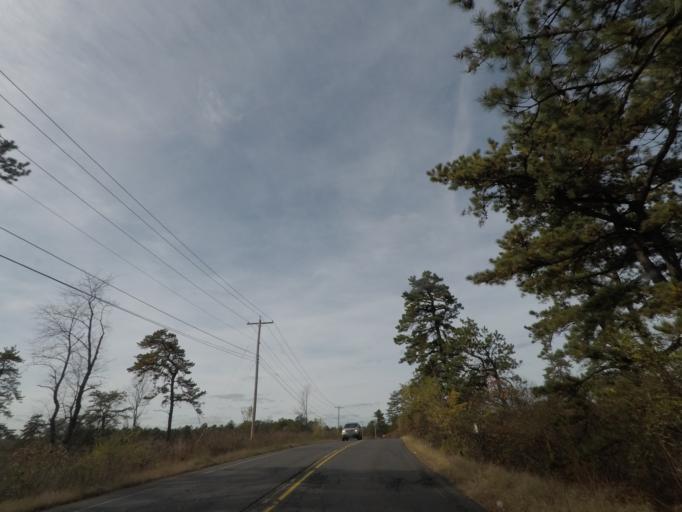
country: US
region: New York
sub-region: Albany County
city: Westmere
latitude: 42.7202
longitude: -73.8697
